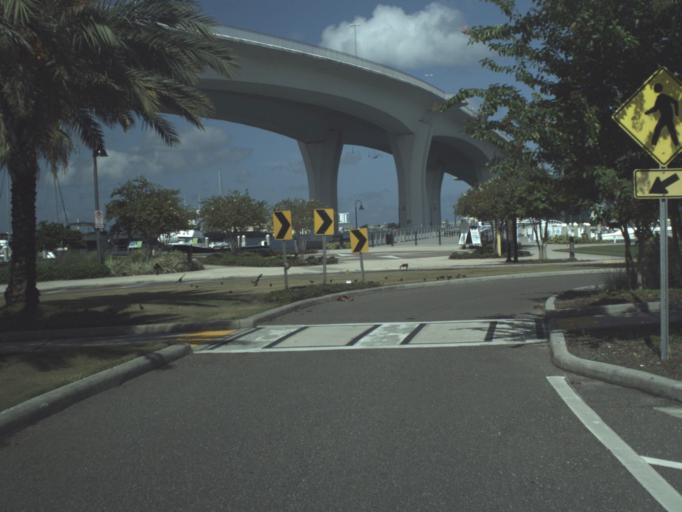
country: US
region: Florida
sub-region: Pinellas County
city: Clearwater
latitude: 27.9657
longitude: -82.8034
